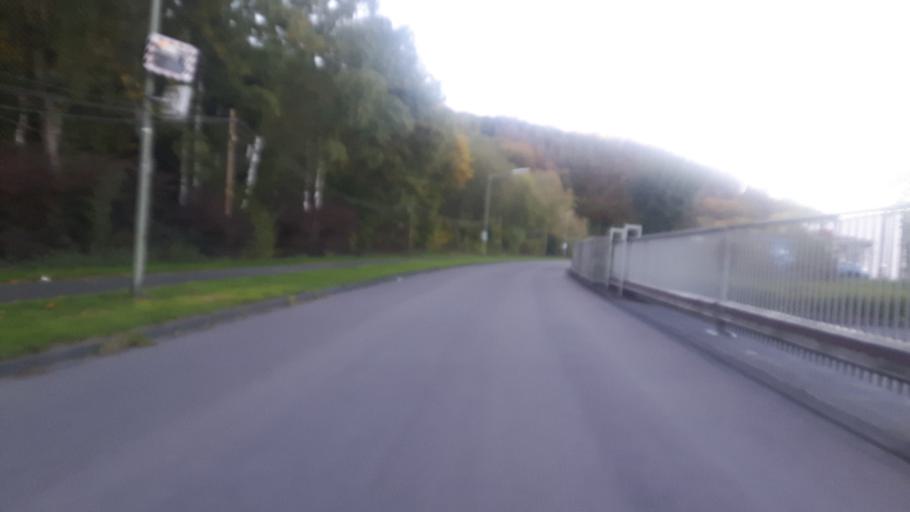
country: DE
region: Rheinland-Pfalz
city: Mudersbach
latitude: 50.8309
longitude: 7.9516
